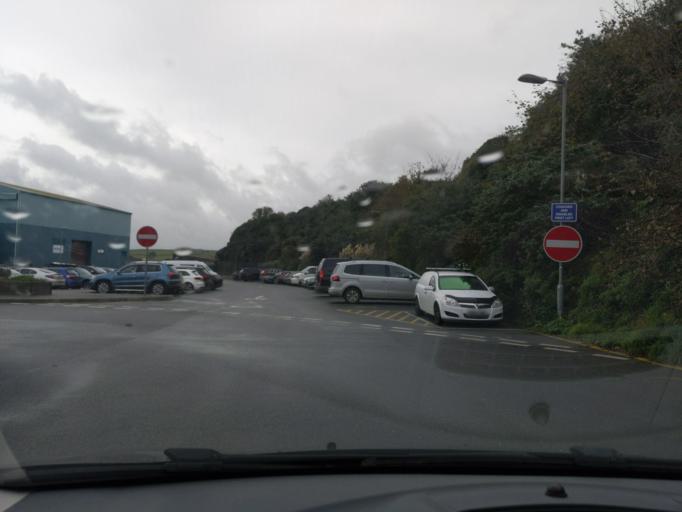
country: GB
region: England
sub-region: Cornwall
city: Padstow
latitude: 50.5384
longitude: -4.9359
